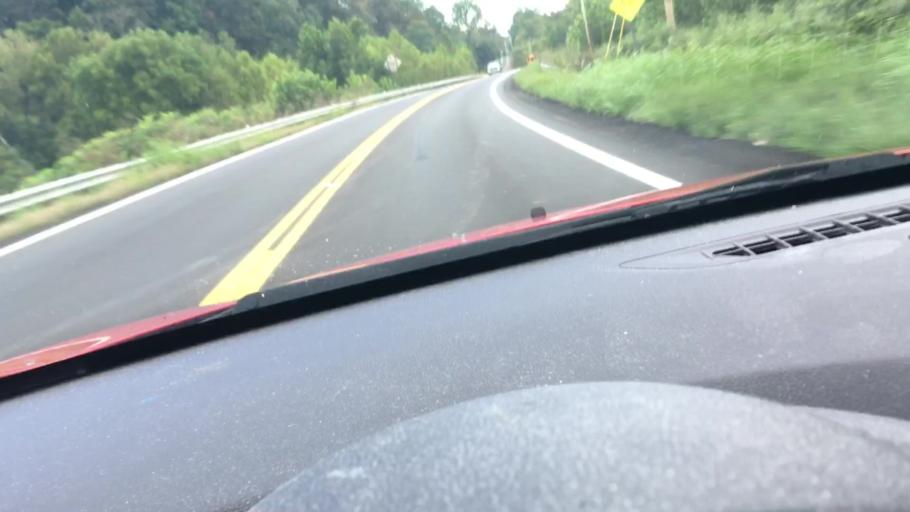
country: US
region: Ohio
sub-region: Athens County
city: Chauncey
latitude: 39.3894
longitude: -82.1419
